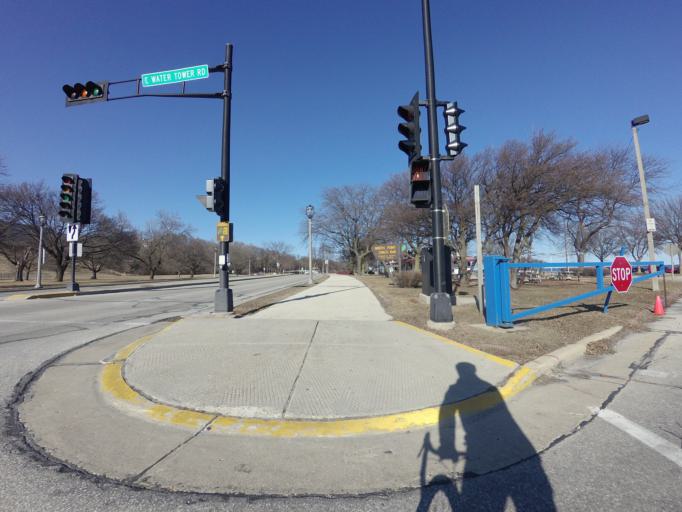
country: US
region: Wisconsin
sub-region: Milwaukee County
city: Shorewood
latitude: 43.0578
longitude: -87.8771
